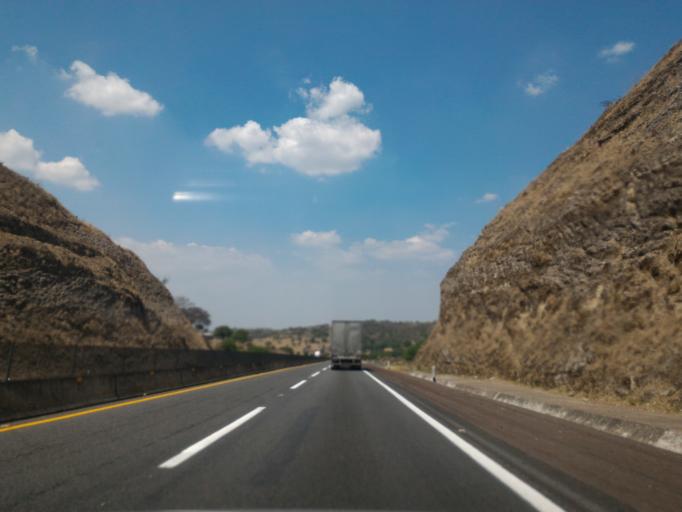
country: MX
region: Jalisco
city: Jalostotitlan
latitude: 21.1300
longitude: -102.4452
